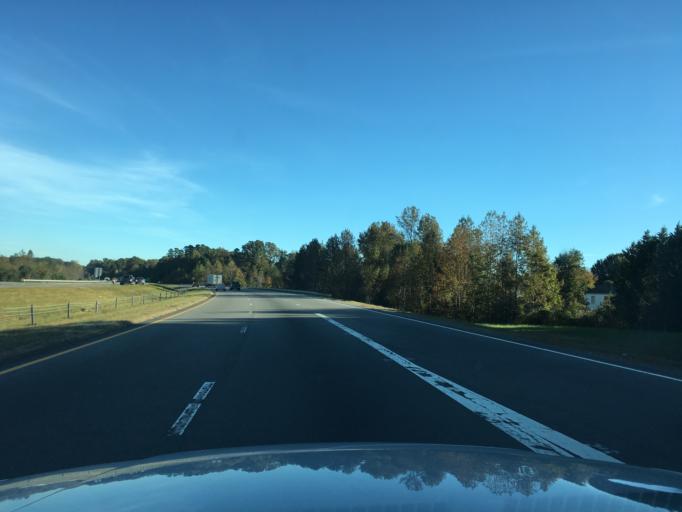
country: US
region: North Carolina
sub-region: Catawba County
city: Mountain View
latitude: 35.6910
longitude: -81.3516
